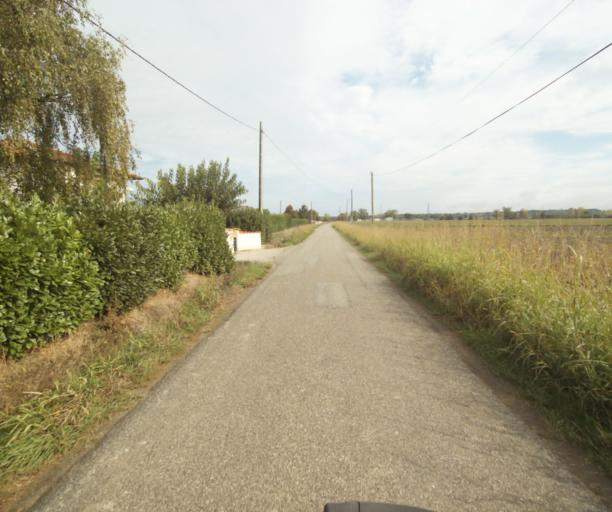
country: FR
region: Midi-Pyrenees
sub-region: Departement du Tarn-et-Garonne
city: Finhan
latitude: 43.9043
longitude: 1.2382
